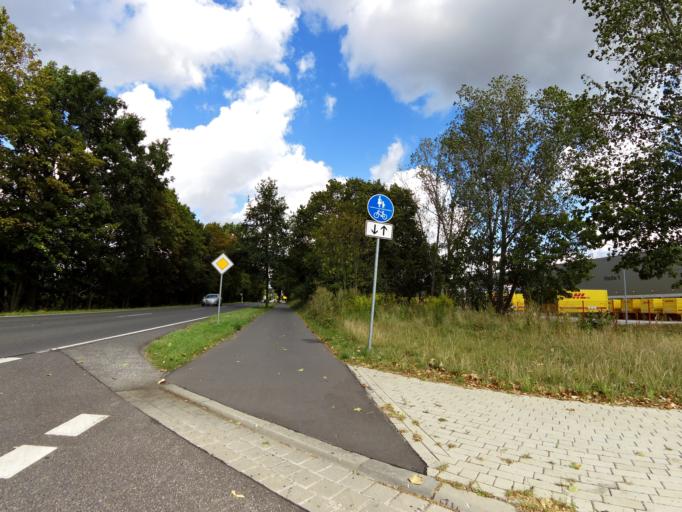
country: DE
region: Brandenburg
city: Grossbeeren
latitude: 52.3772
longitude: 13.3241
